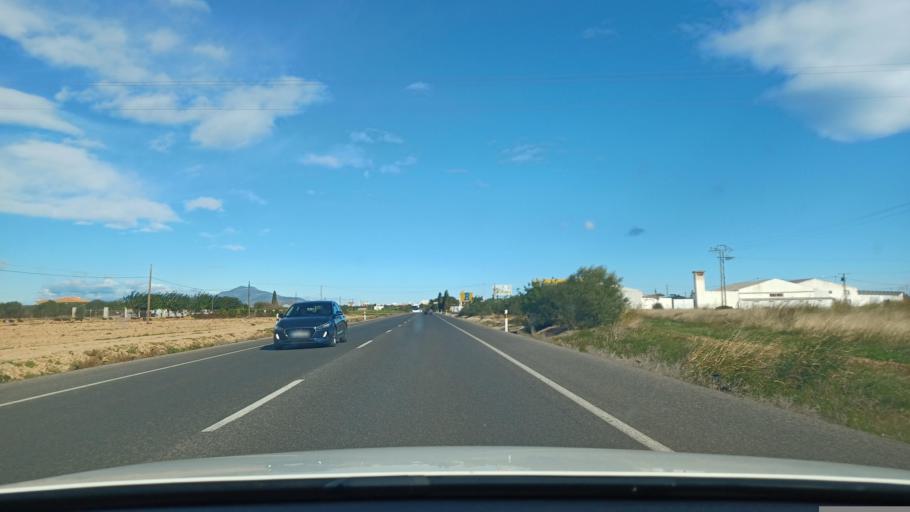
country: ES
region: Valencia
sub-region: Provincia de Castello
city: Benicarlo
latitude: 40.4420
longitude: 0.4441
